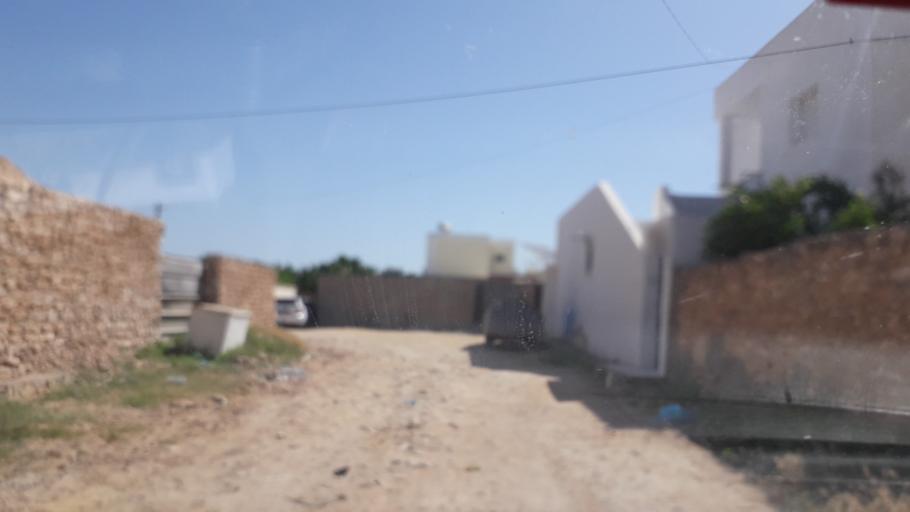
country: TN
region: Safaqis
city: Al Qarmadah
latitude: 34.8091
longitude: 10.7686
